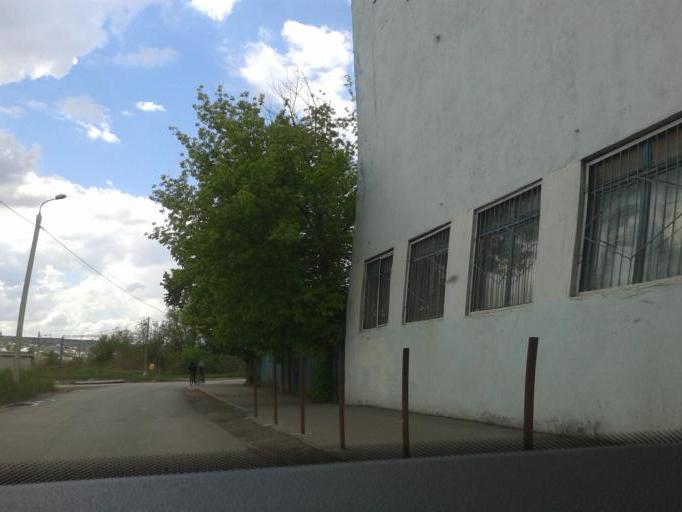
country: RU
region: Volgograd
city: Krasnoslobodsk
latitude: 48.5166
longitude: 44.5203
